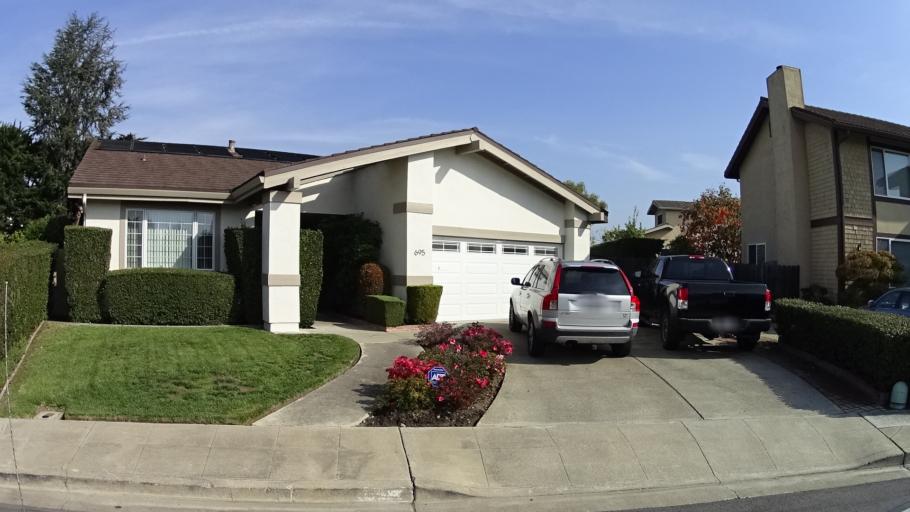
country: US
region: California
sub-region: San Mateo County
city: Foster City
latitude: 37.5521
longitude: -122.2782
